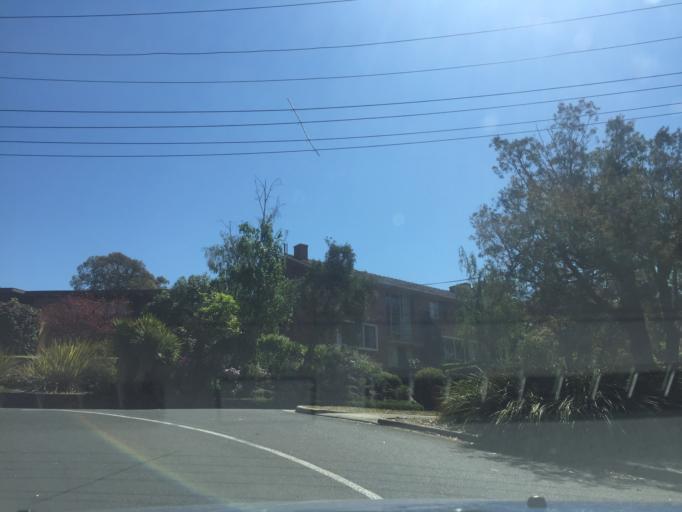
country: AU
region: Victoria
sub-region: Manningham
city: Bulleen
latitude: -37.7695
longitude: 145.0669
